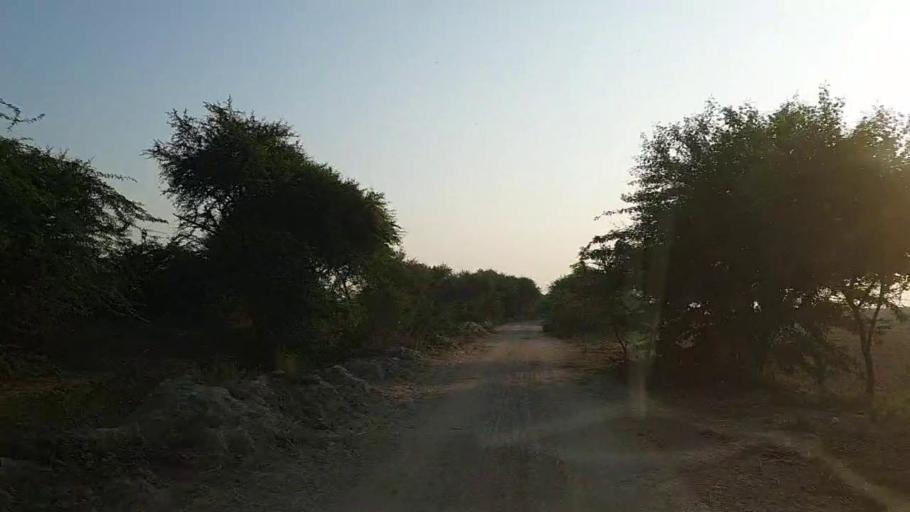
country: PK
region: Sindh
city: Daro Mehar
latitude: 24.7407
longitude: 68.1844
